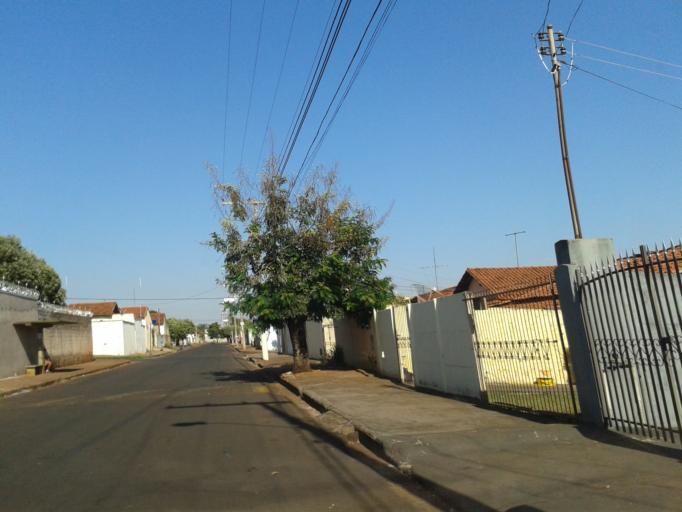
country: BR
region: Minas Gerais
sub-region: Ituiutaba
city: Ituiutaba
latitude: -18.9689
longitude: -49.4854
